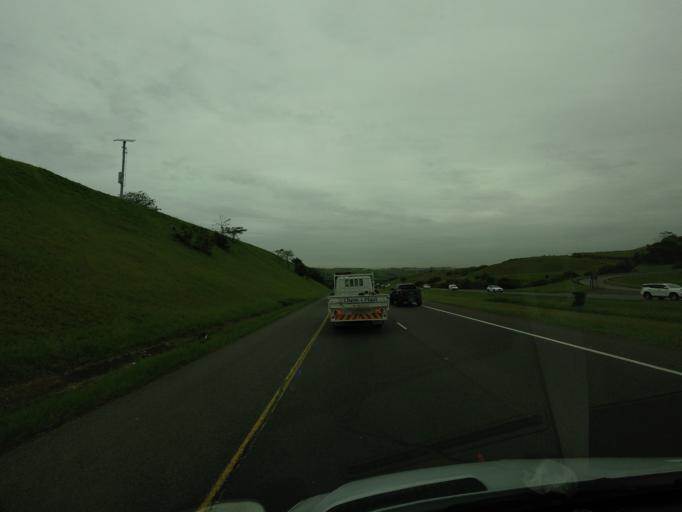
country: ZA
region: KwaZulu-Natal
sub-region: eThekwini Metropolitan Municipality
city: Durban
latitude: -29.6849
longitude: 31.0883
